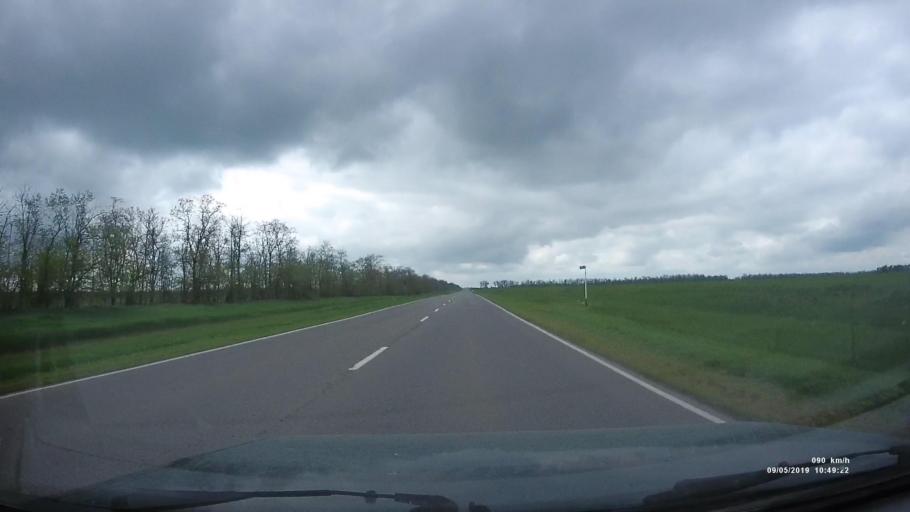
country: RU
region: Rostov
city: Peshkovo
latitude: 46.9435
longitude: 39.3555
